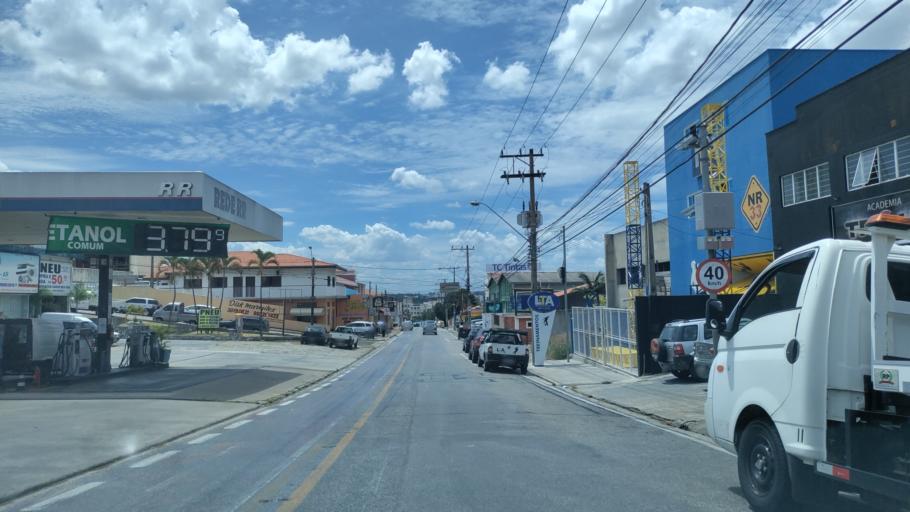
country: BR
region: Sao Paulo
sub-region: Sorocaba
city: Sorocaba
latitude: -23.4776
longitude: -47.4618
